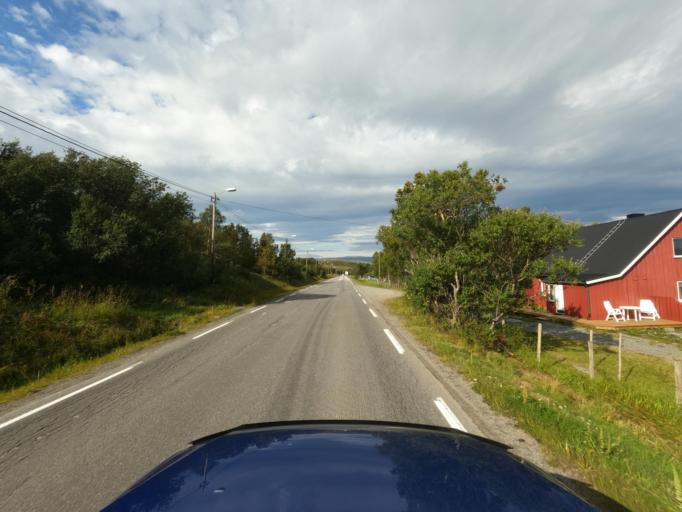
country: NO
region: Finnmark Fylke
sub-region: Kvalsund
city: Kvalsund
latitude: 70.5015
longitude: 24.0649
